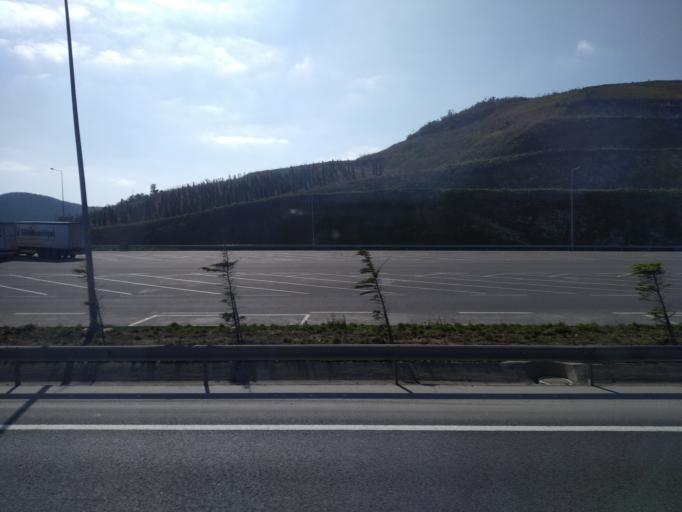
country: TR
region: Istanbul
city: Arikoey
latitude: 41.2248
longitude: 28.9857
